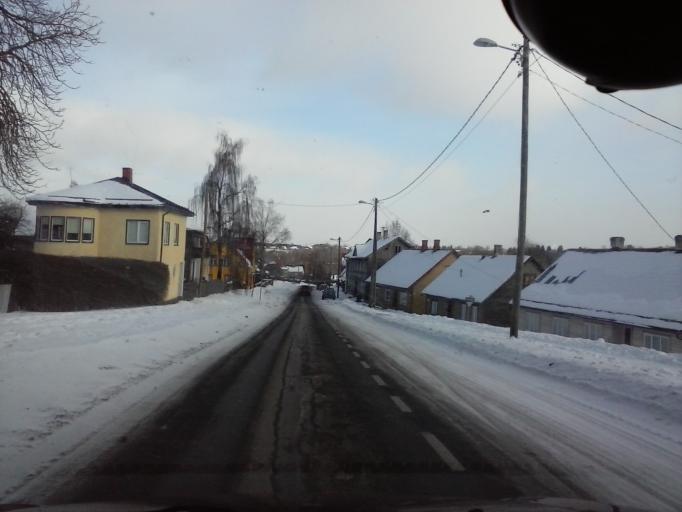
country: EE
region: Viljandimaa
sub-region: Viiratsi vald
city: Viiratsi
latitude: 58.3653
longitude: 25.6159
